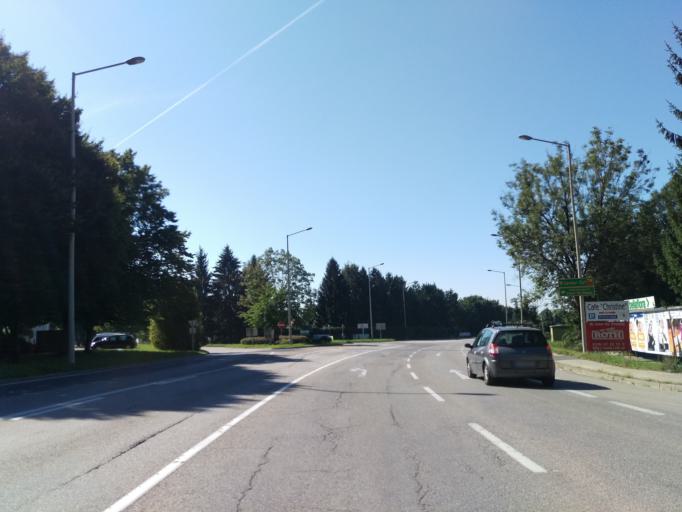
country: AT
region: Styria
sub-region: Politischer Bezirk Graz-Umgebung
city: Raaba
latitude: 47.0405
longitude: 15.4885
